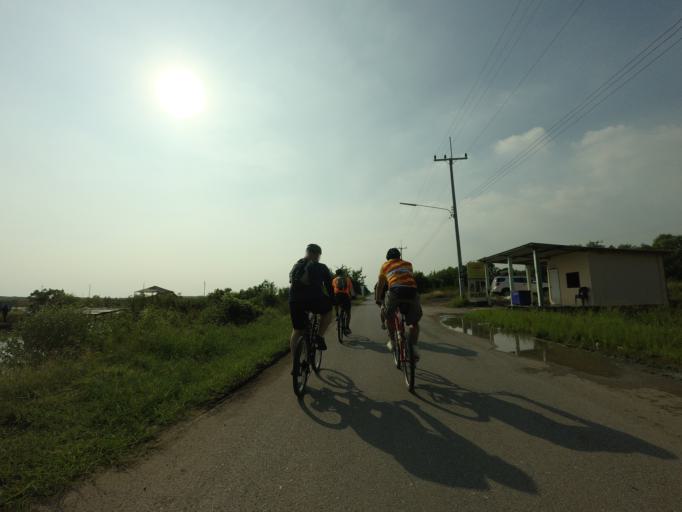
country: TH
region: Samut Sakhon
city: Samut Sakhon
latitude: 13.4989
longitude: 100.3571
